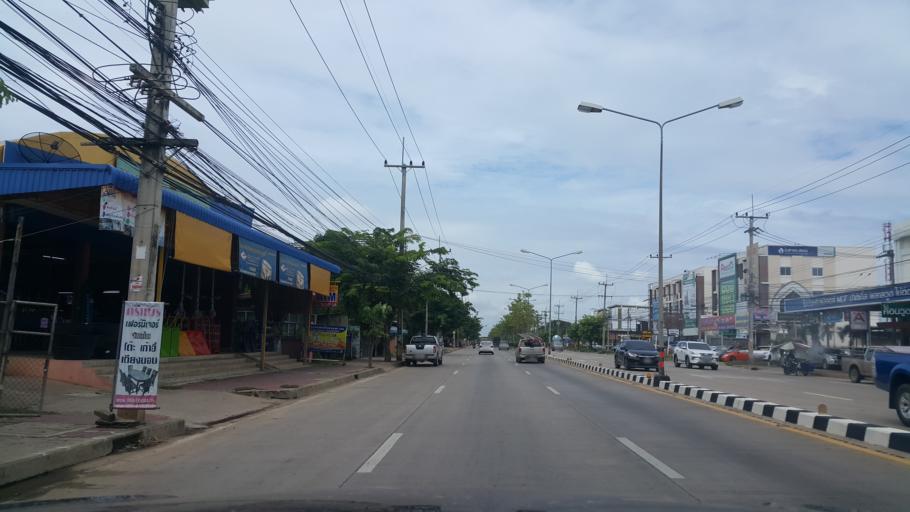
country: TH
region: Phitsanulok
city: Phitsanulok
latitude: 16.8181
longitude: 100.2415
